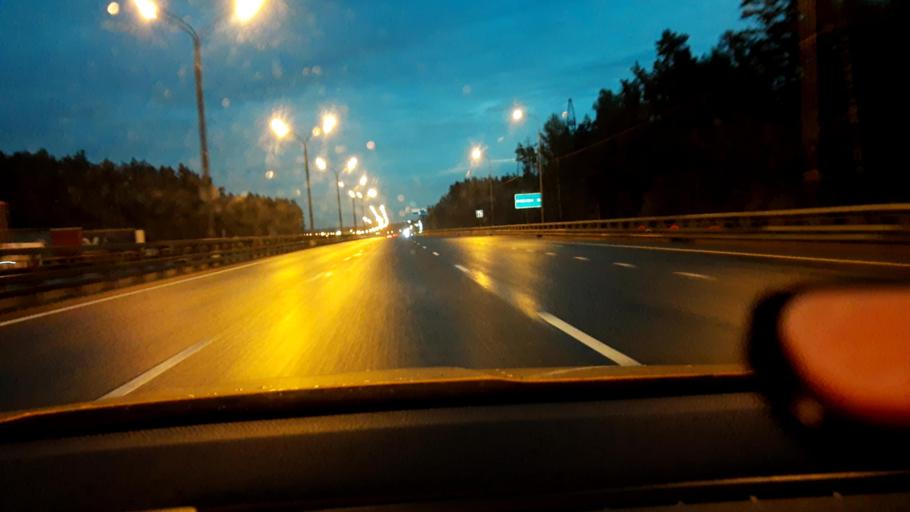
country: RU
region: Moskovskaya
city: Lesnoy Gorodok
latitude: 55.6254
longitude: 37.1818
